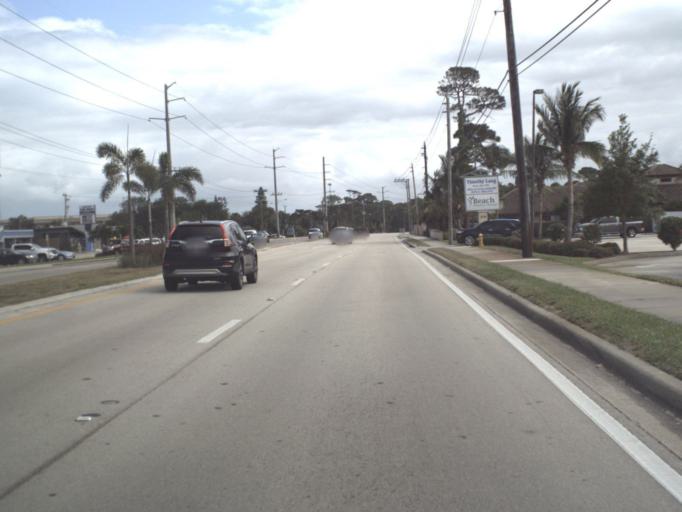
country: US
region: Florida
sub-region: Brevard County
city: Indian Harbour Beach
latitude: 28.1480
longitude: -80.5994
